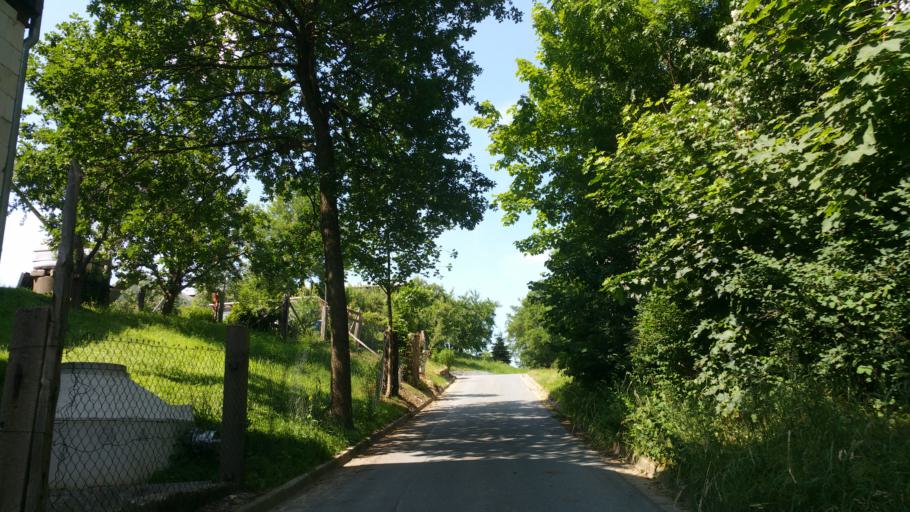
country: DE
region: Bavaria
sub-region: Upper Franconia
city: Schwarzenbach an der Saale
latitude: 50.2102
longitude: 11.9050
